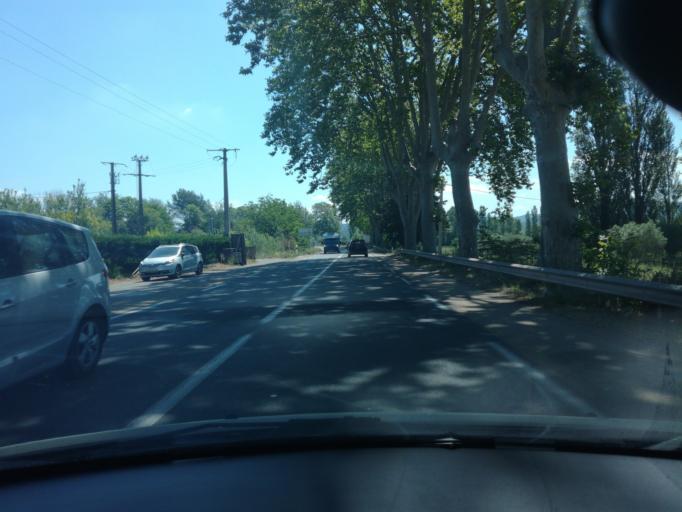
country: FR
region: Provence-Alpes-Cote d'Azur
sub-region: Departement du Var
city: Les Arcs
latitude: 43.4475
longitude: 6.4798
